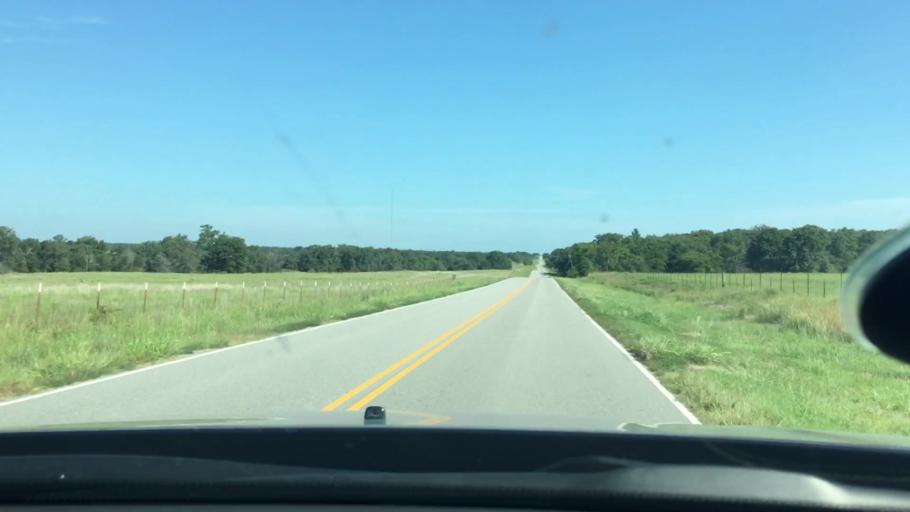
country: US
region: Oklahoma
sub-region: Johnston County
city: Tishomingo
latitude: 34.3074
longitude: -96.5488
